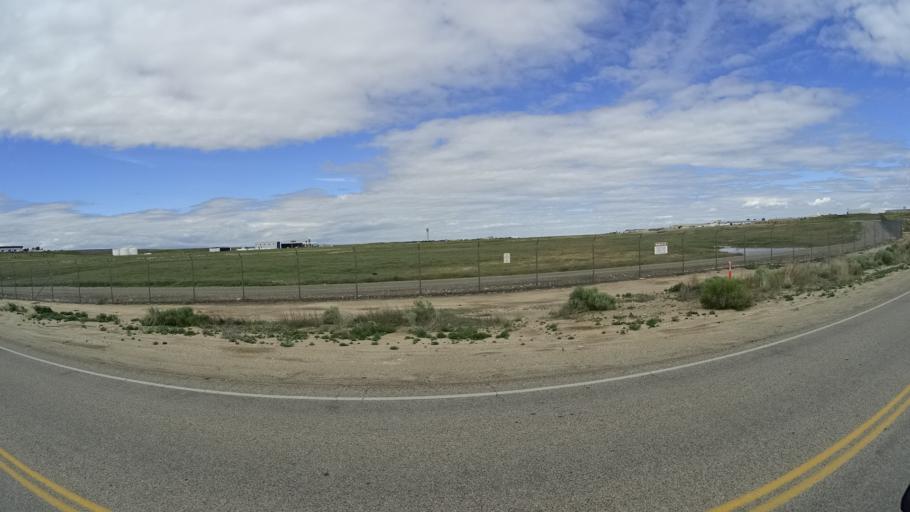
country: US
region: Idaho
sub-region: Ada County
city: Boise
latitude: 43.5533
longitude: -116.1871
